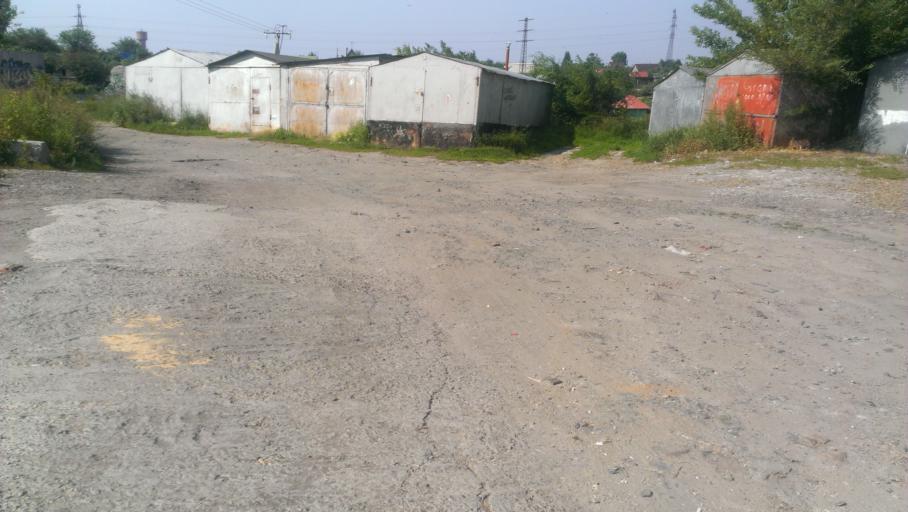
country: RU
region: Altai Krai
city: Novosilikatnyy
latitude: 53.3839
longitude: 83.6708
